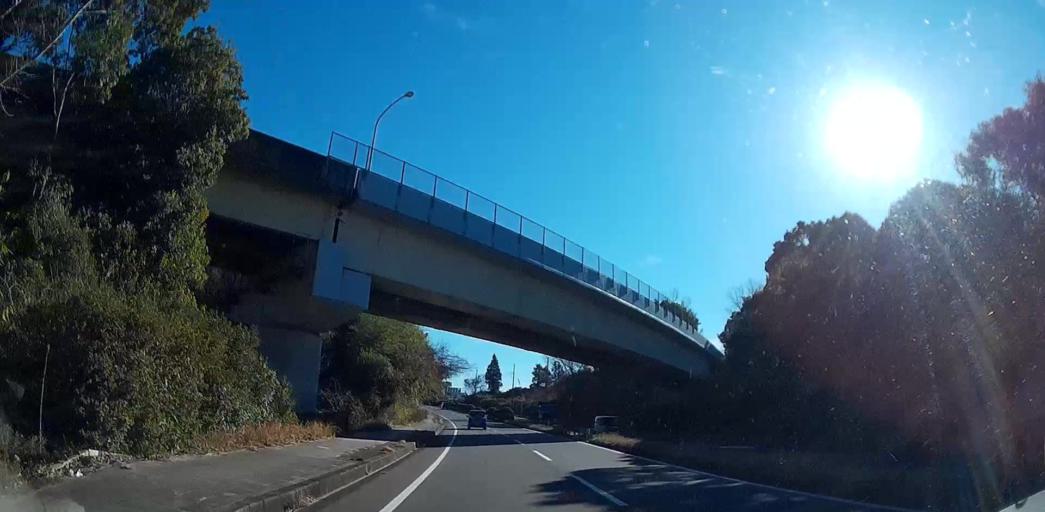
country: JP
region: Chiba
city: Narita
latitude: 35.7838
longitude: 140.3459
